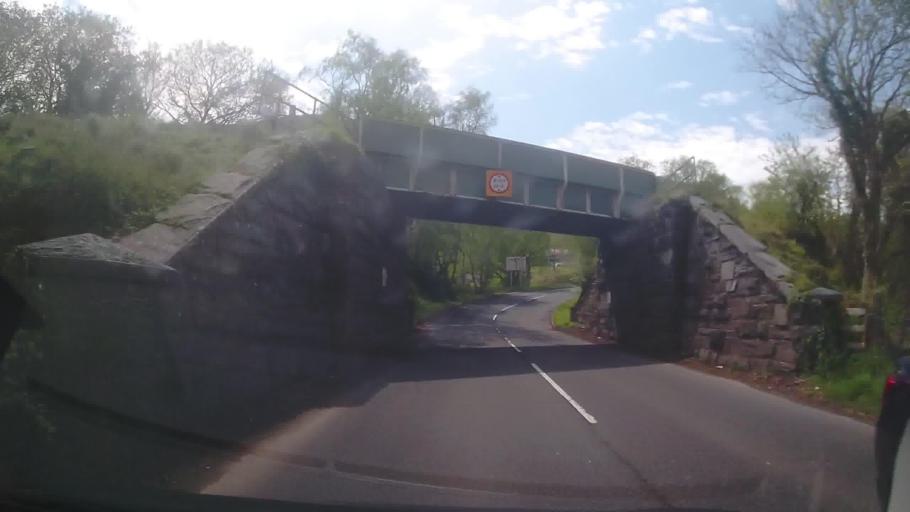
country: GB
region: Wales
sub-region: Gwynedd
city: Porthmadog
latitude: 52.9344
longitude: -4.1530
